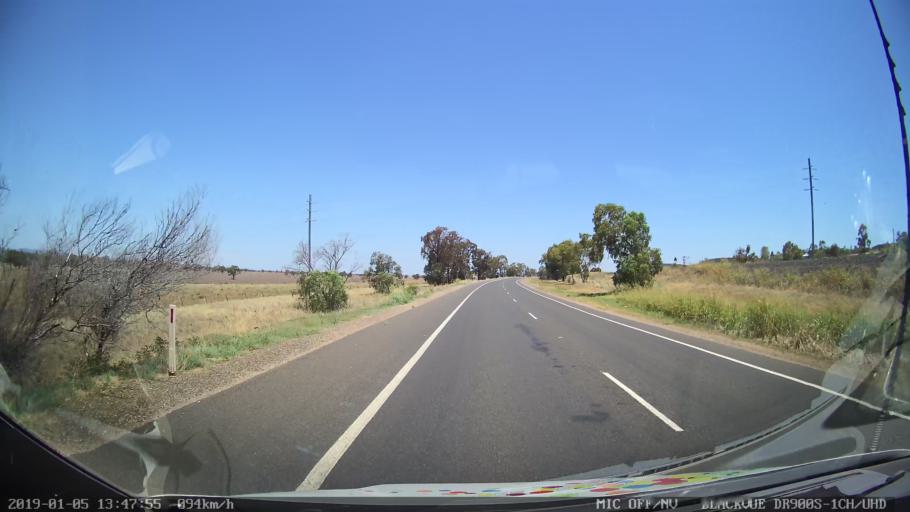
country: AU
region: New South Wales
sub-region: Gunnedah
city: Gunnedah
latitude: -30.9942
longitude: 150.2793
